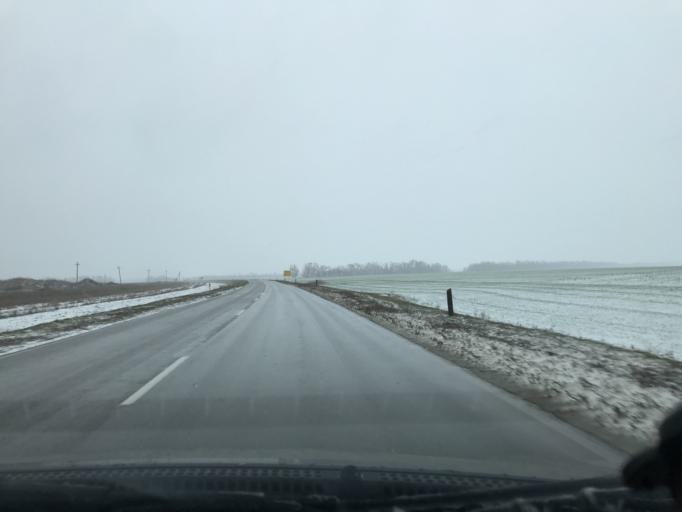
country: RU
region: Rostov
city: Yegorlykskaya
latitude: 46.5471
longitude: 40.6548
